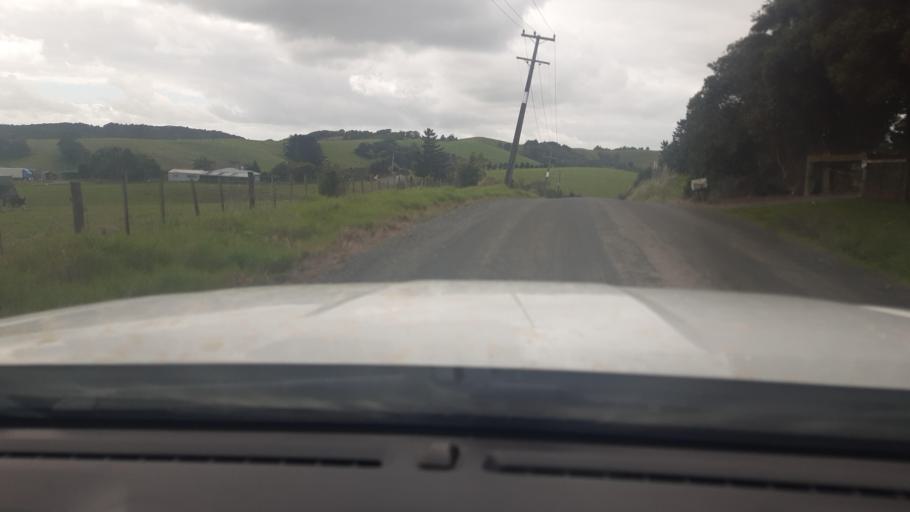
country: NZ
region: Northland
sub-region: Far North District
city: Kaitaia
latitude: -35.0953
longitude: 173.3141
